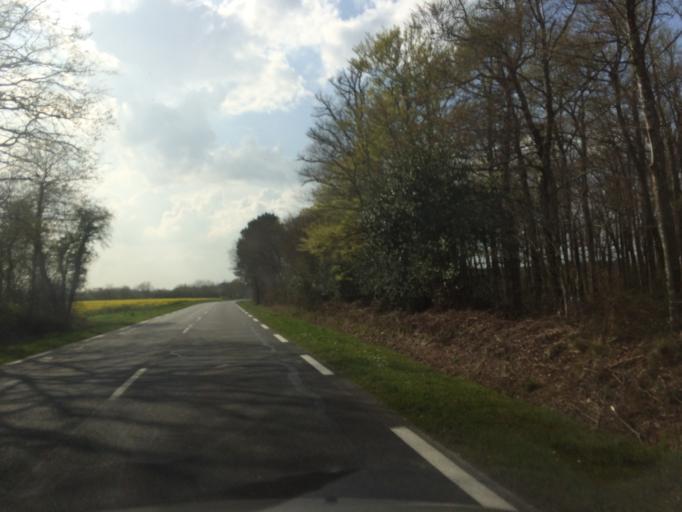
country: FR
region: Pays de la Loire
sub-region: Departement de la Loire-Atlantique
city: Bouvron
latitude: 47.4853
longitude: -1.8404
